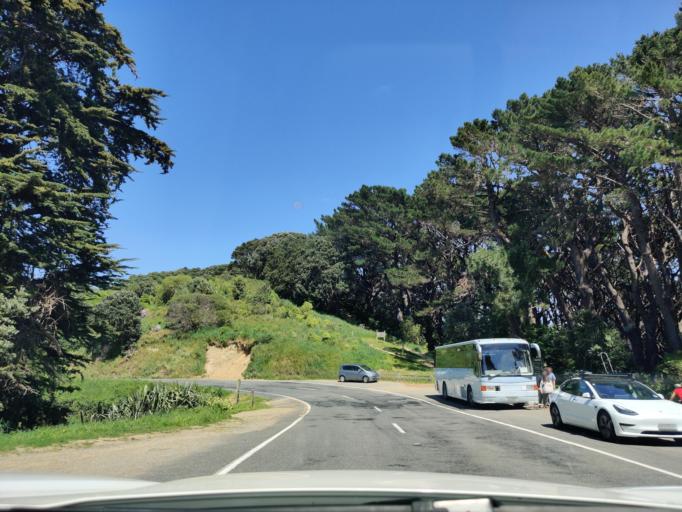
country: NZ
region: Wellington
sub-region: Wellington City
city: Wellington
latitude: -41.3026
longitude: 174.7895
